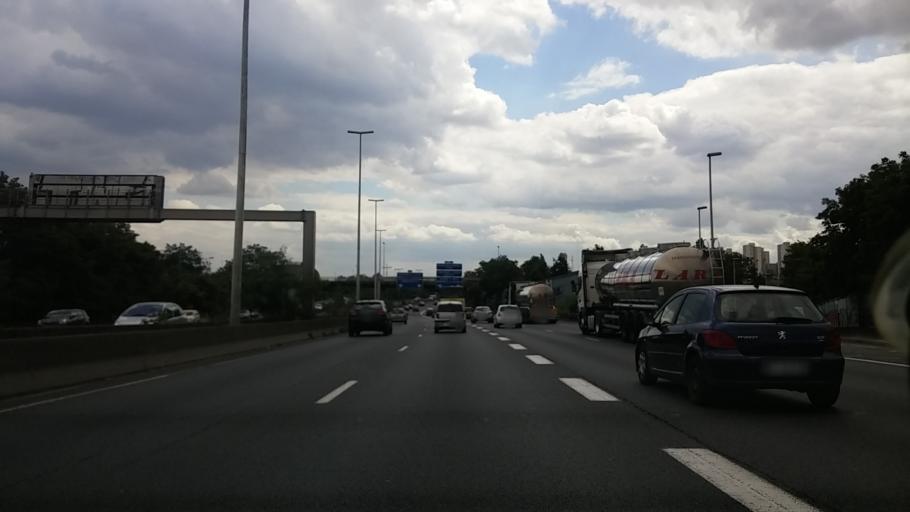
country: FR
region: Ile-de-France
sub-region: Departement de Seine-Saint-Denis
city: Noisy-le-Sec
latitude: 48.8901
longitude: 2.4736
